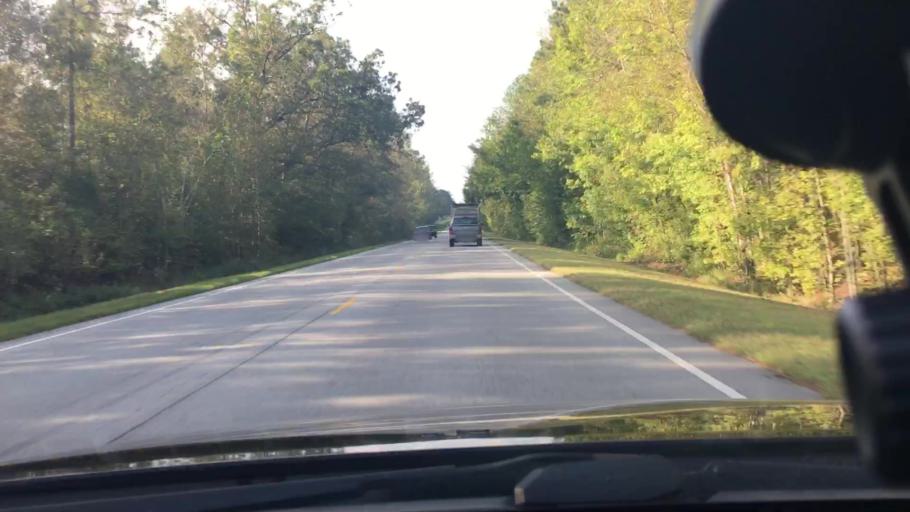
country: US
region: North Carolina
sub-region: Craven County
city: Vanceboro
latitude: 35.3115
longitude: -77.1392
